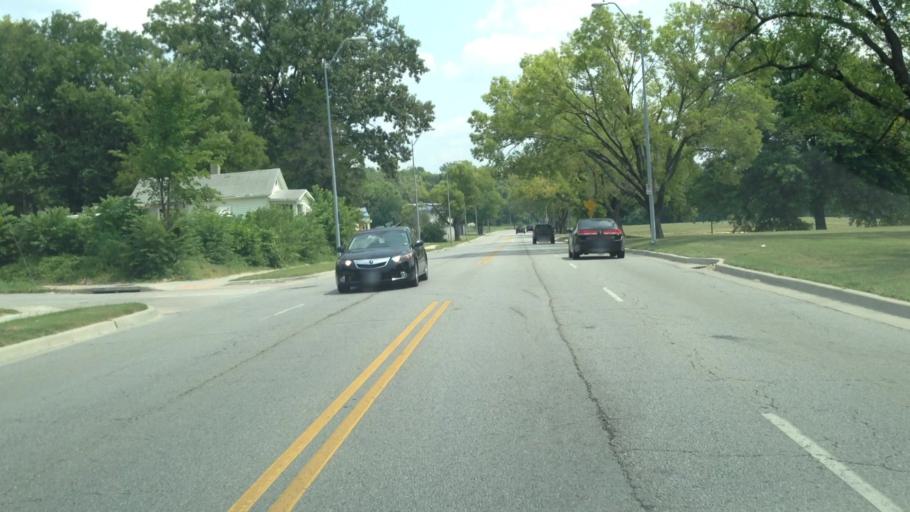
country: US
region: Missouri
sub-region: Jackson County
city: Kansas City
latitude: 39.0408
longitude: -94.5514
